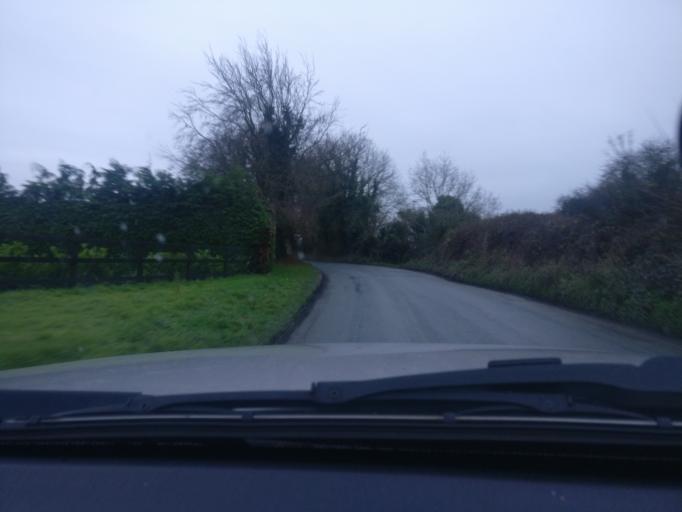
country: IE
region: Leinster
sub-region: Kildare
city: Kilcock
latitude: 53.4442
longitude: -6.6240
